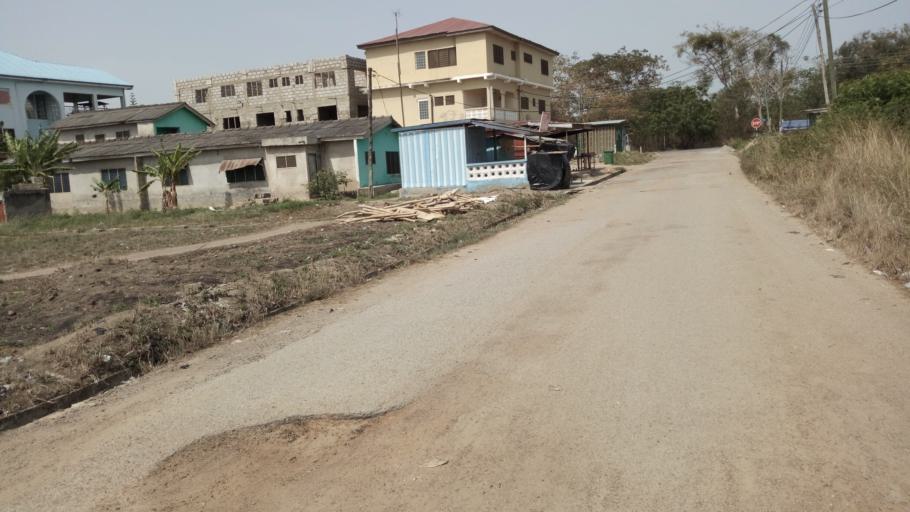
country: GH
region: Central
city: Winneba
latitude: 5.3633
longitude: -0.6360
